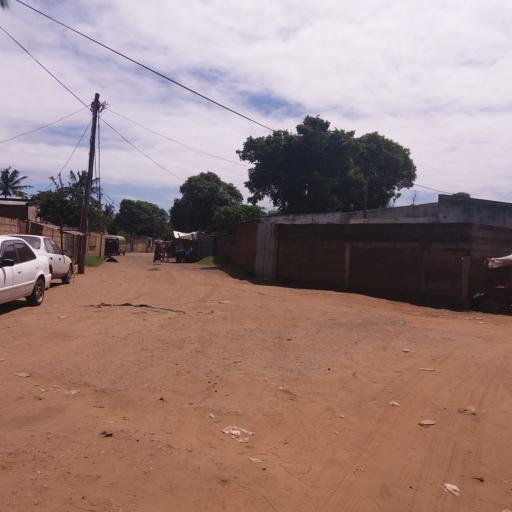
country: MZ
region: Maputo City
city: Maputo
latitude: -25.9092
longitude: 32.5905
